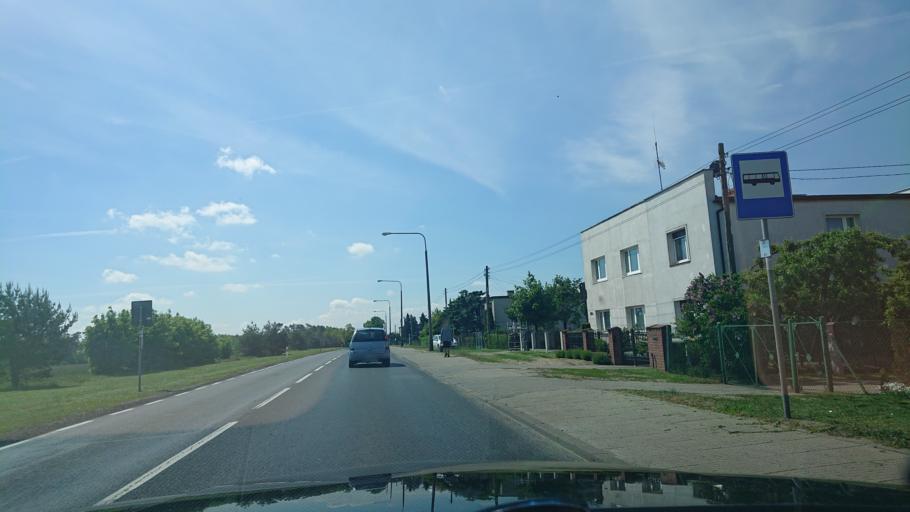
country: PL
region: Greater Poland Voivodeship
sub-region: Powiat gnieznienski
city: Gniezno
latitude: 52.5104
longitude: 17.5950
